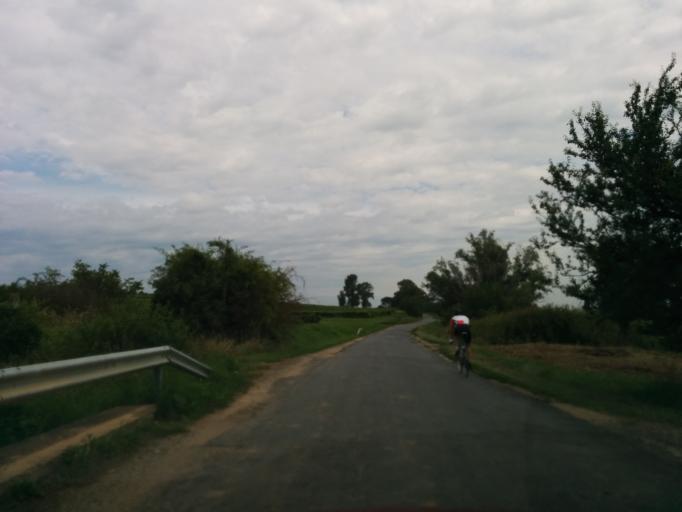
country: HU
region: Gyor-Moson-Sopron
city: Fertorakos
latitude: 47.6652
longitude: 16.6691
